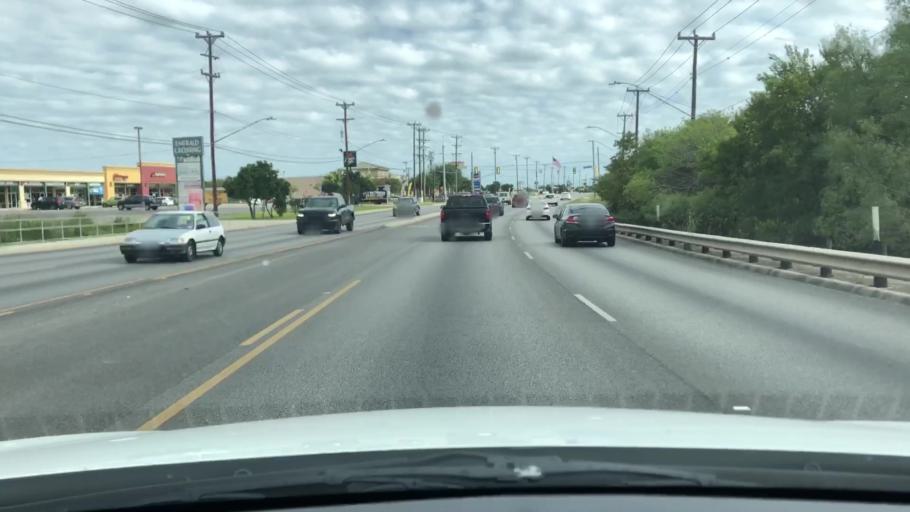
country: US
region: Texas
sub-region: Bexar County
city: Leon Valley
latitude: 29.4907
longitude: -98.6835
